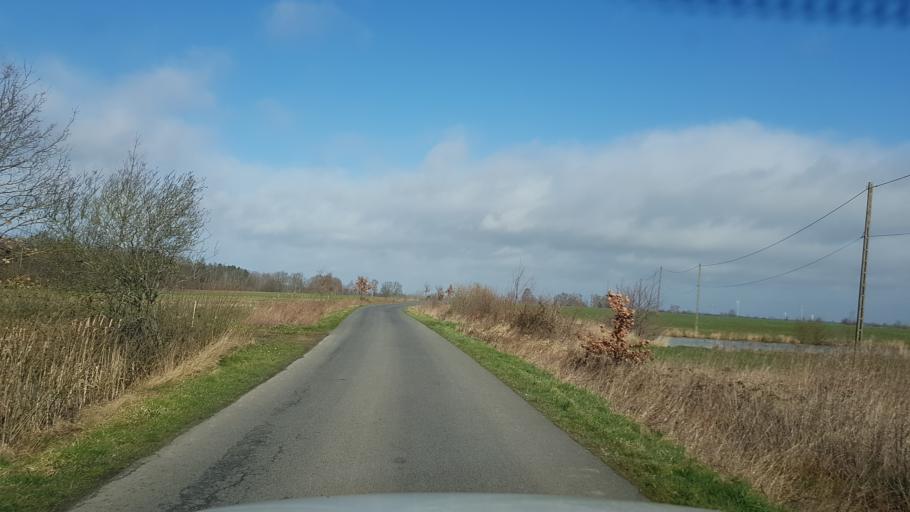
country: PL
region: West Pomeranian Voivodeship
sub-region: Powiat slawienski
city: Slawno
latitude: 54.4933
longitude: 16.6495
